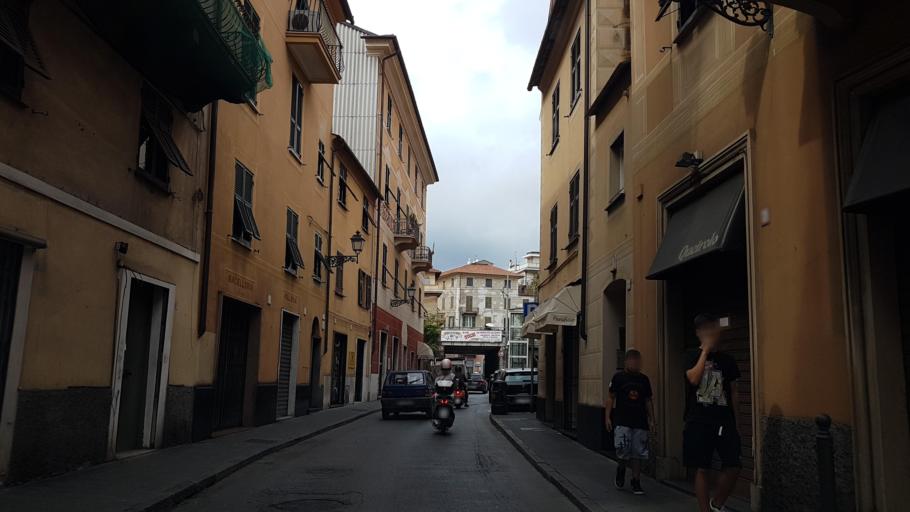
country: IT
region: Liguria
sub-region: Provincia di Genova
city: Rapallo
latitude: 44.3506
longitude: 9.2276
